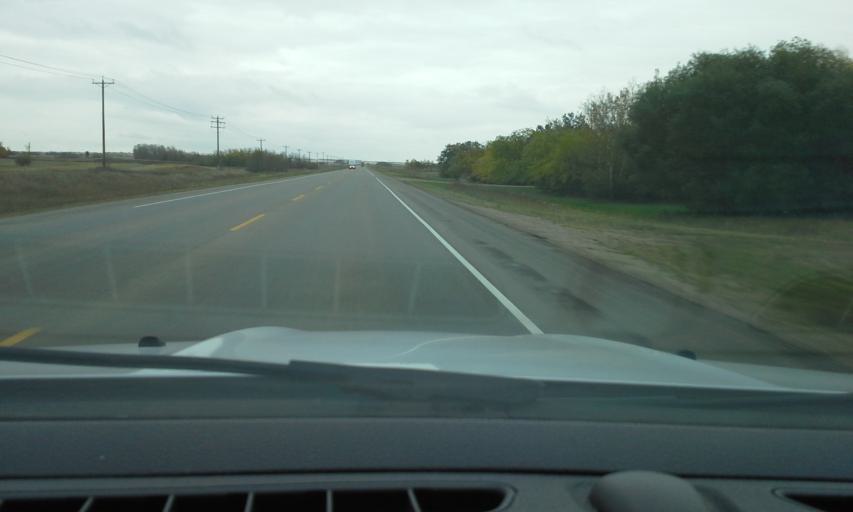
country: CA
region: Saskatchewan
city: Lloydminster
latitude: 53.2780
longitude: -109.8285
